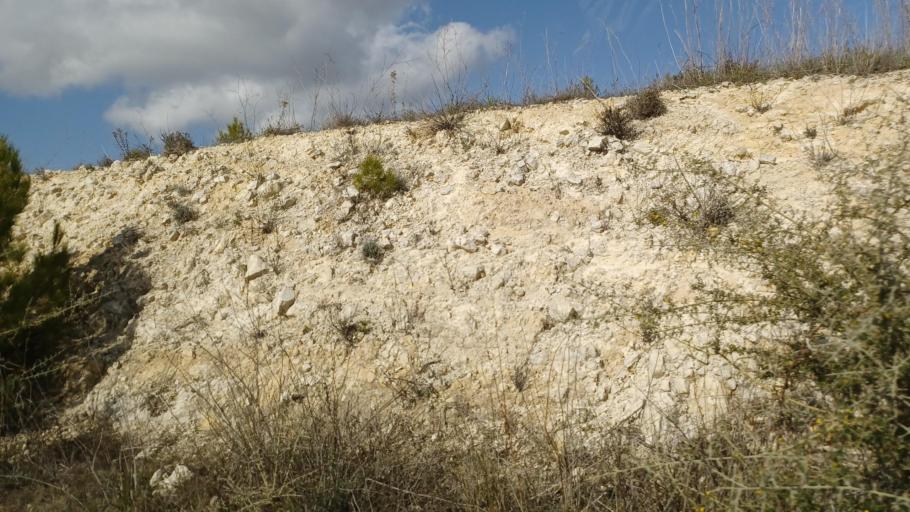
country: CY
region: Limassol
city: Pachna
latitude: 34.8436
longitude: 32.7155
